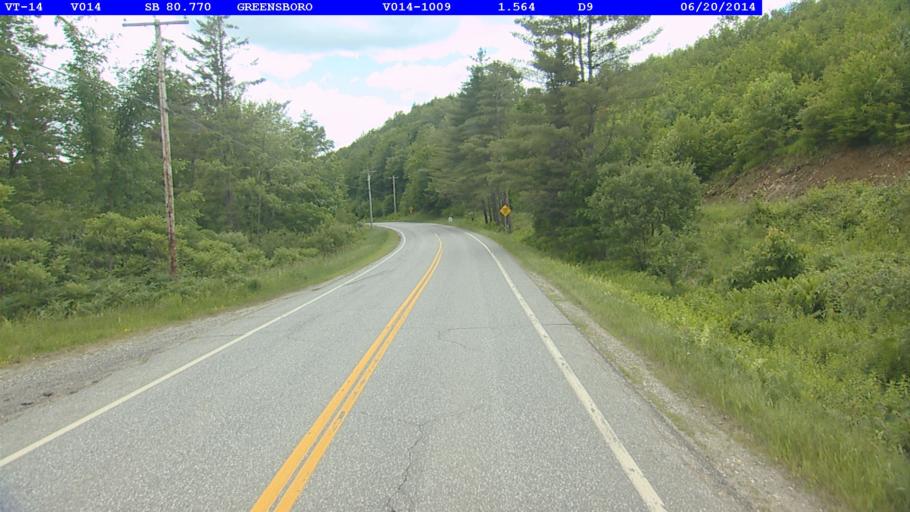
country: US
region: Vermont
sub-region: Caledonia County
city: Hardwick
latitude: 44.6014
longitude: -72.3586
